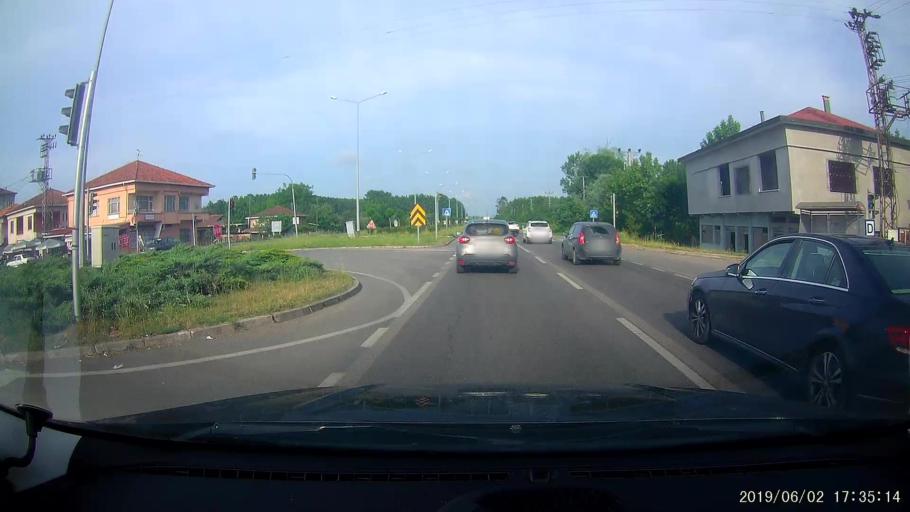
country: TR
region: Samsun
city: Terme
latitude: 41.2196
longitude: 36.8811
